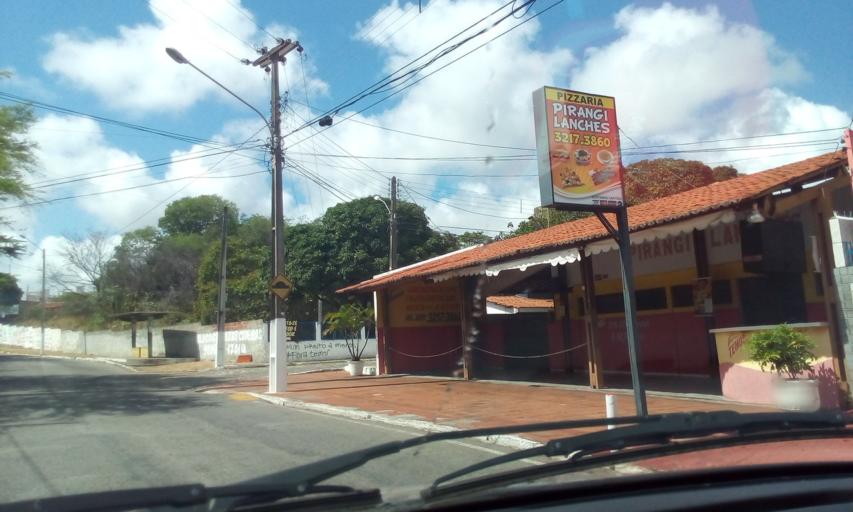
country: BR
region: Rio Grande do Norte
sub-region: Parnamirim
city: Parnamirim
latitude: -5.8724
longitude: -35.2087
